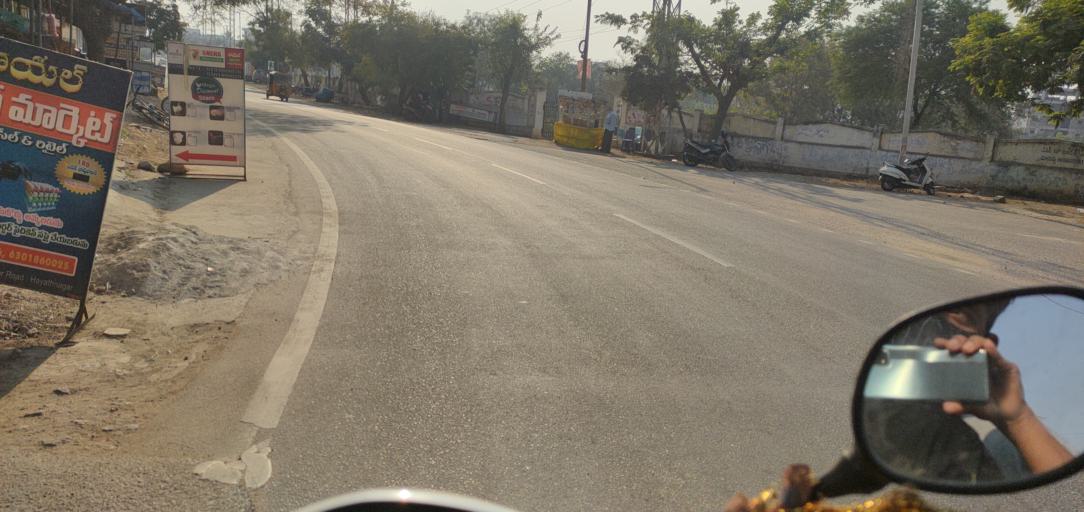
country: IN
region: Telangana
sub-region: Rangareddi
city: Lal Bahadur Nagar
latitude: 17.3362
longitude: 78.6145
